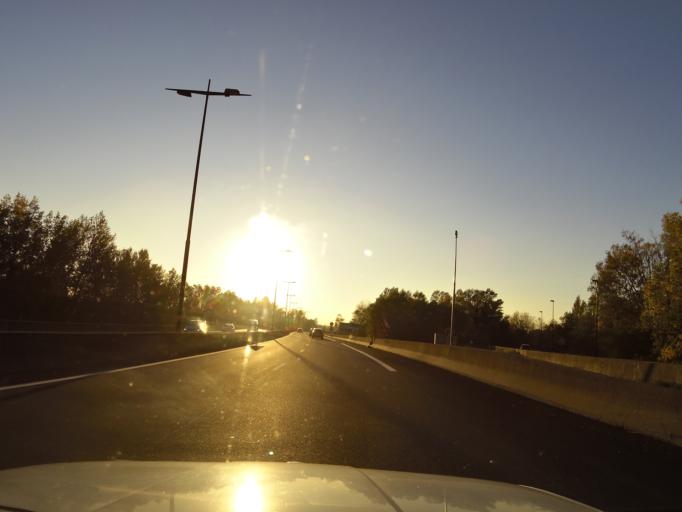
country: FR
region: Rhone-Alpes
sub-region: Departement du Rhone
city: Vaulx-en-Velin
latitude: 45.7967
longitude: 4.9368
